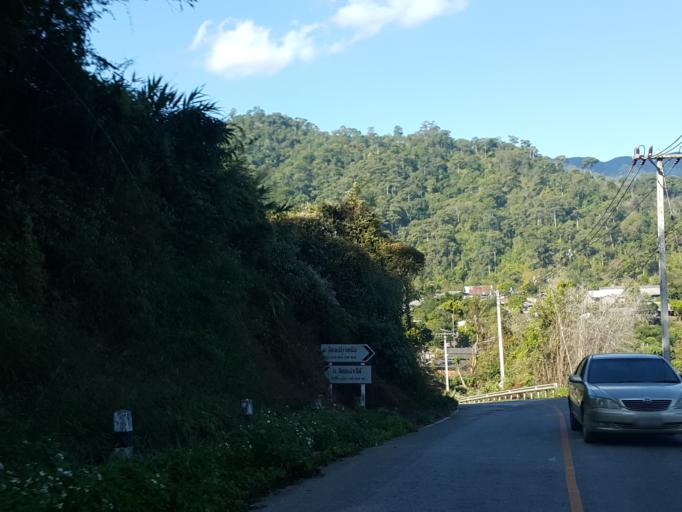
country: TH
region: Chiang Mai
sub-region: Amphoe Chiang Dao
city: Chiang Dao
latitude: 19.5247
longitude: 98.8640
